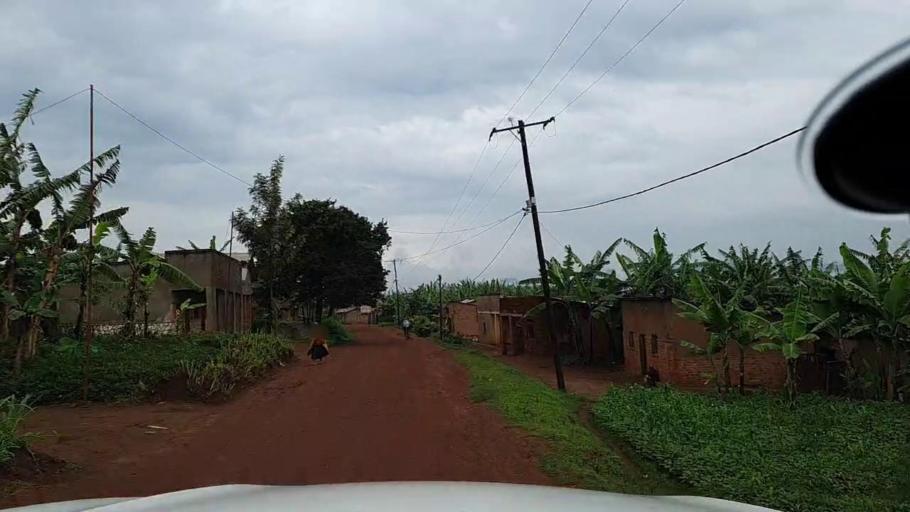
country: RW
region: Kigali
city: Kigali
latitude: -1.9131
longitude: 29.8985
